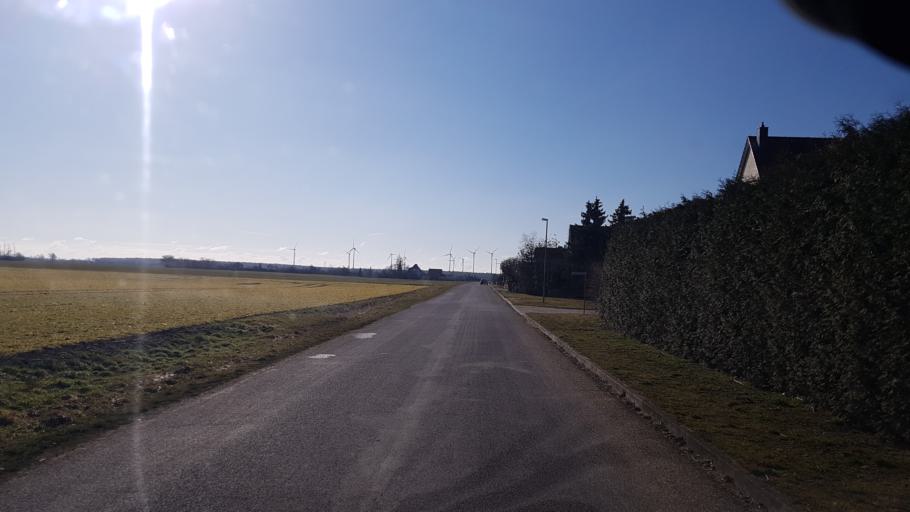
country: DE
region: Brandenburg
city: Muhlberg
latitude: 51.5024
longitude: 13.2320
